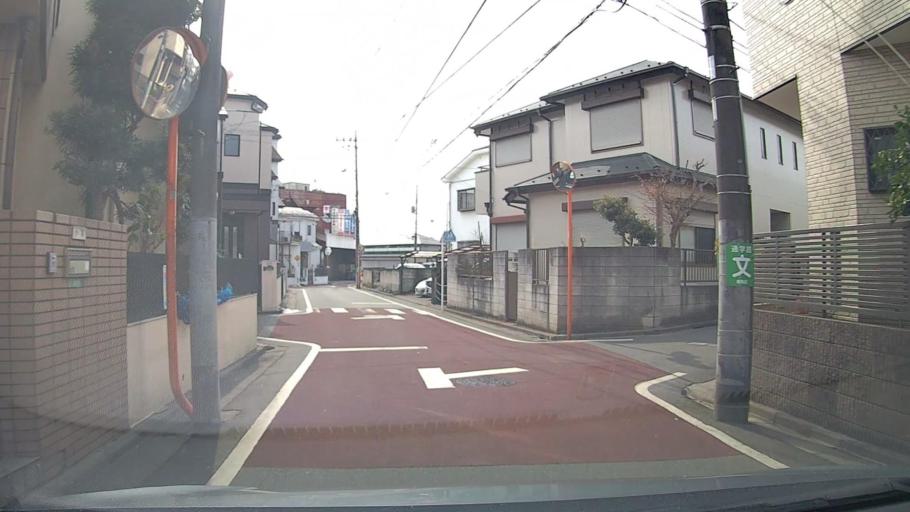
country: JP
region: Tokyo
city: Nishi-Tokyo-shi
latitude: 35.7585
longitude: 139.5717
